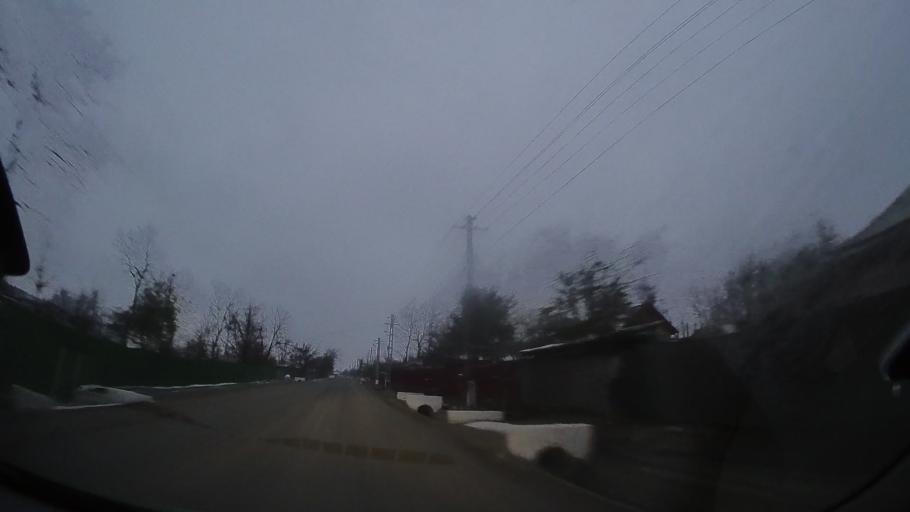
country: RO
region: Vaslui
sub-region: Comuna Gagesti
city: Gagesti
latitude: 46.3902
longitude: 27.9812
